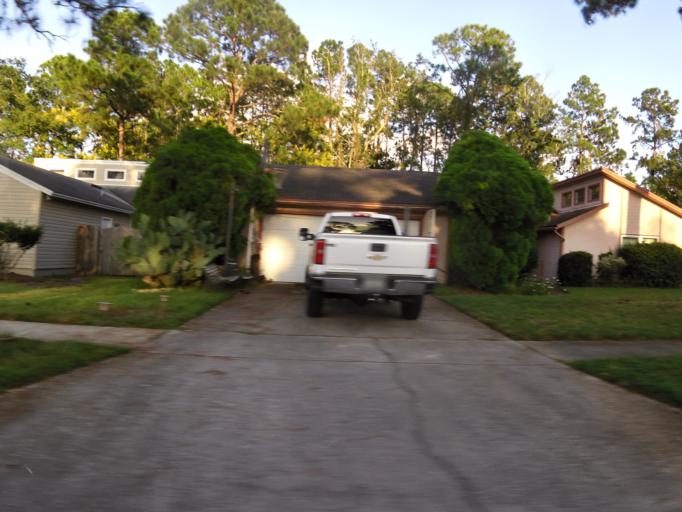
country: US
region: Florida
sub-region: Clay County
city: Orange Park
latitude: 30.2014
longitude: -81.6219
